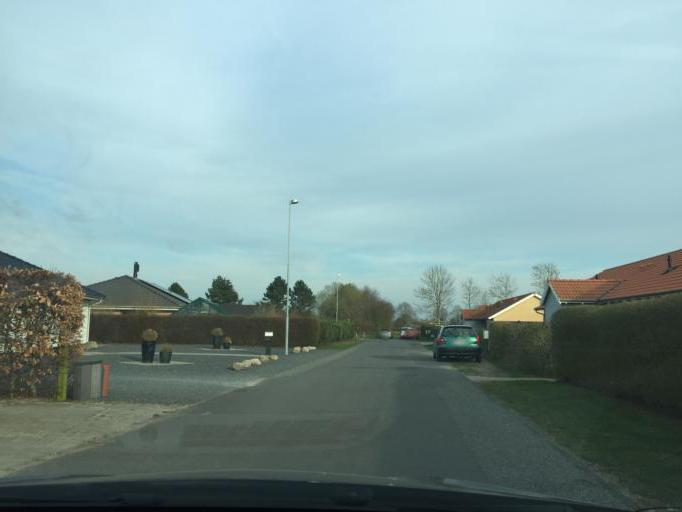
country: DK
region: South Denmark
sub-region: Kerteminde Kommune
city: Langeskov
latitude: 55.3225
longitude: 10.5709
